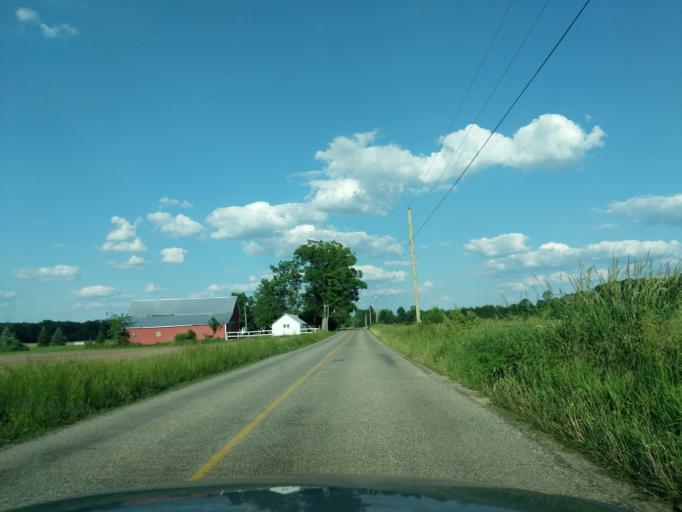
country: US
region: Indiana
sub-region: Whitley County
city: Tri-Lakes
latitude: 41.3022
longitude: -85.5230
